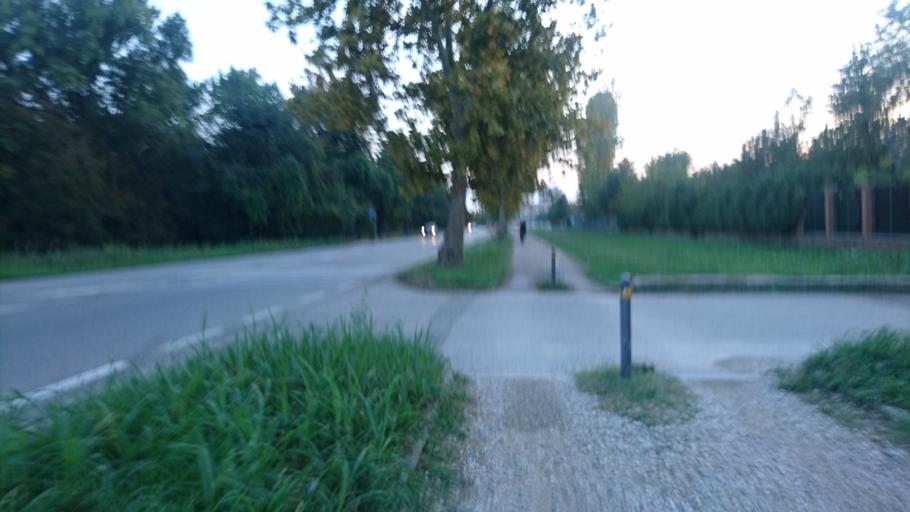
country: IT
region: Emilia-Romagna
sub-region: Provincia di Ferrara
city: Ferrara
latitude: 44.8506
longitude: 11.6153
